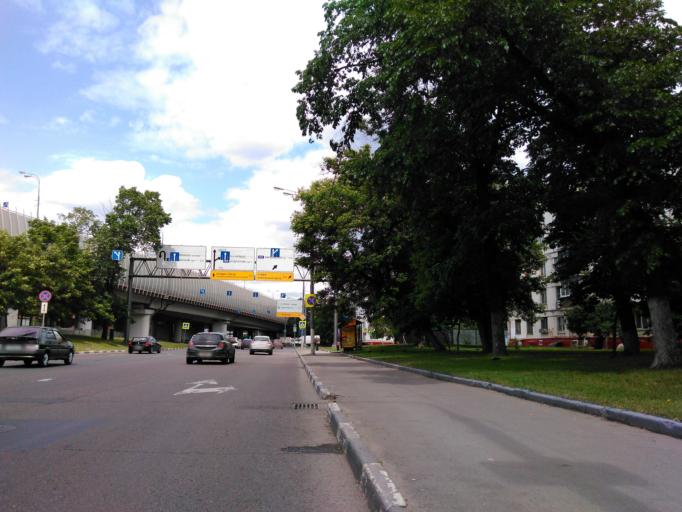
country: RU
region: Moscow
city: Novyye Cheremushki
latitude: 55.7023
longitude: 37.6167
